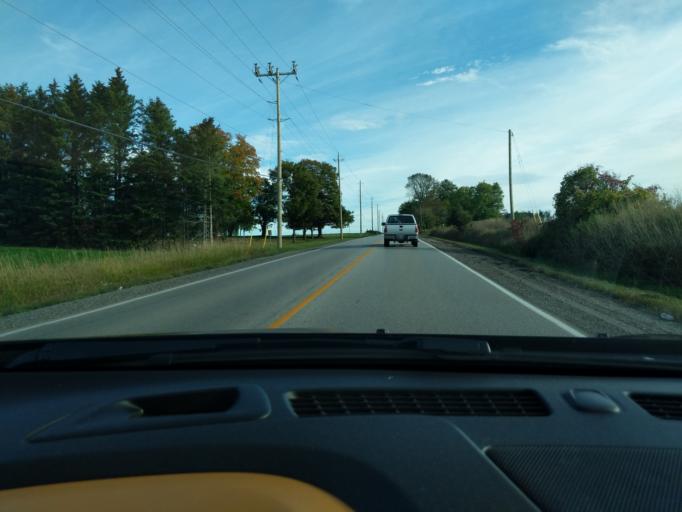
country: CA
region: Ontario
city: Barrie
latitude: 44.4195
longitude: -79.7579
